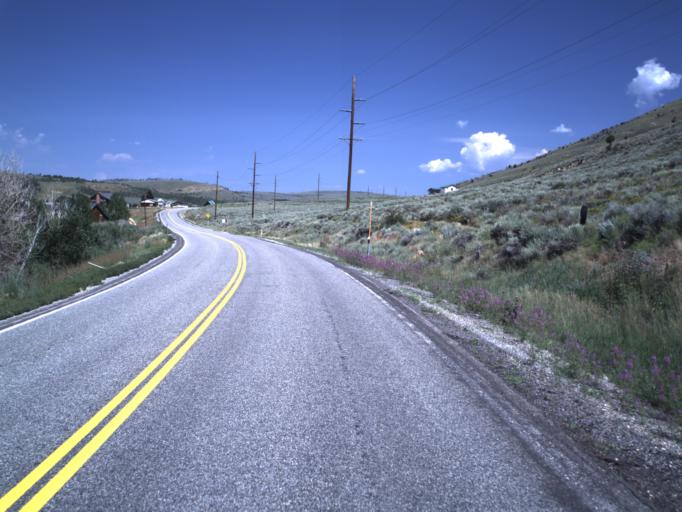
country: US
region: Utah
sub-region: Carbon County
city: Helper
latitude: 39.7972
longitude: -111.1323
